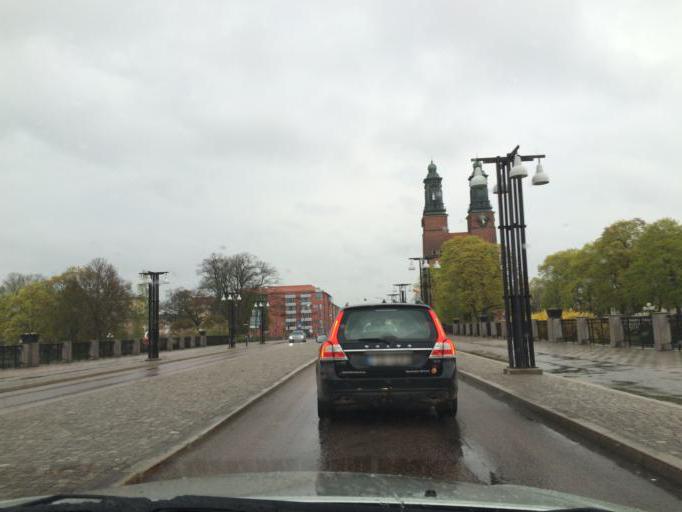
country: SE
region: Soedermanland
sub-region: Eskilstuna Kommun
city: Eskilstuna
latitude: 59.3733
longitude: 16.5157
